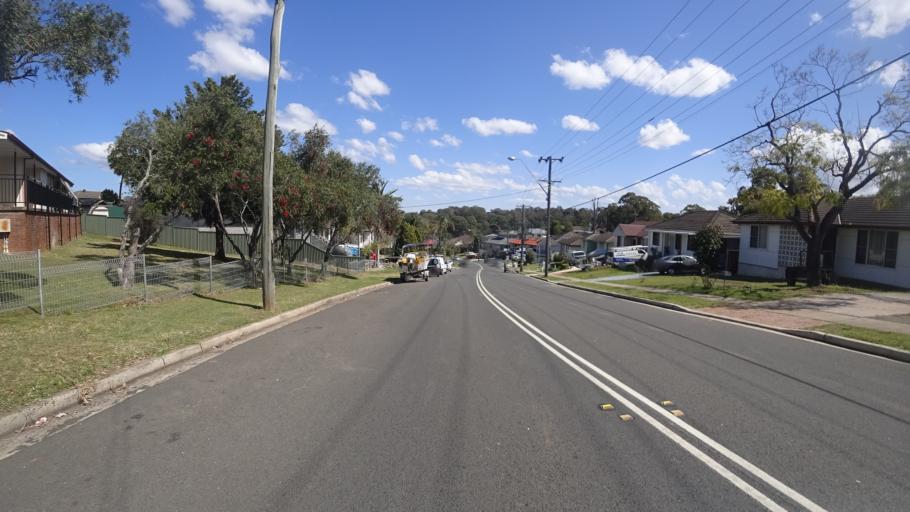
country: AU
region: New South Wales
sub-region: Fairfield
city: Cabramatta West
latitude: -33.9026
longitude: 150.9083
